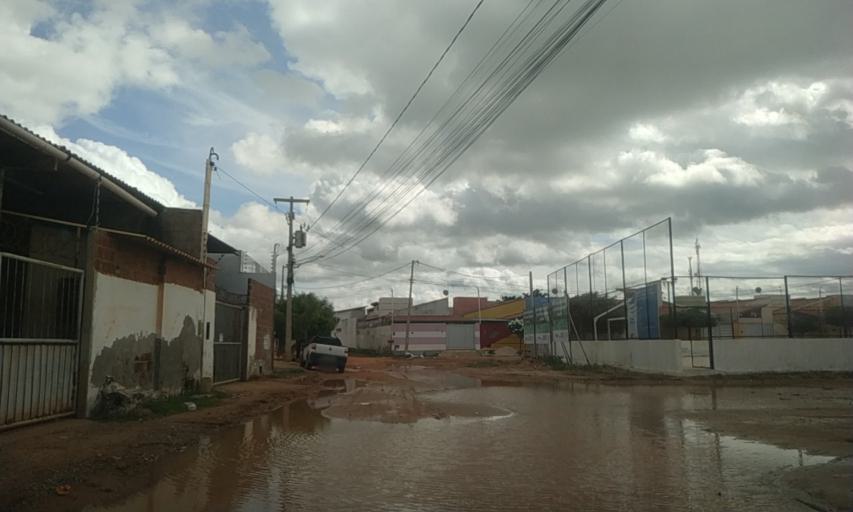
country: BR
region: Rio Grande do Norte
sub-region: Areia Branca
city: Areia Branca
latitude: -4.9536
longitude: -37.1223
